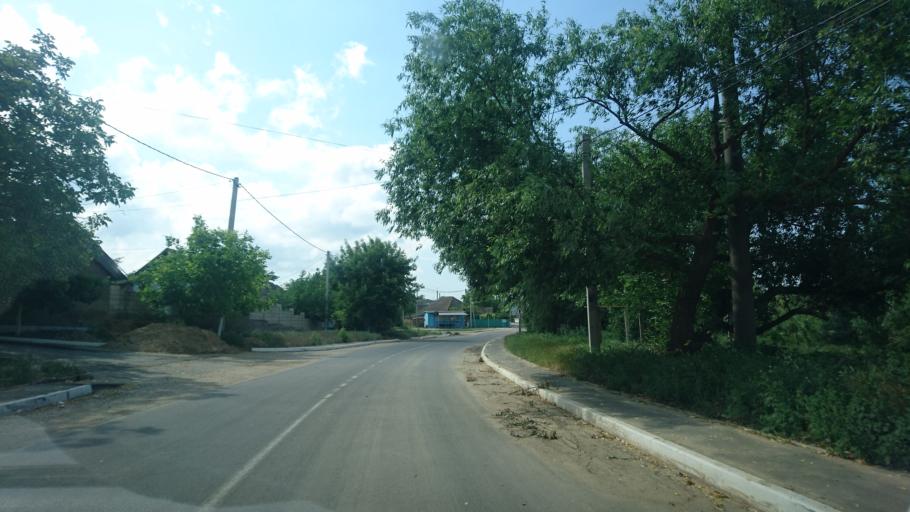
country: MD
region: Telenesti
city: Cocieri
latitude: 47.3516
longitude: 29.1078
